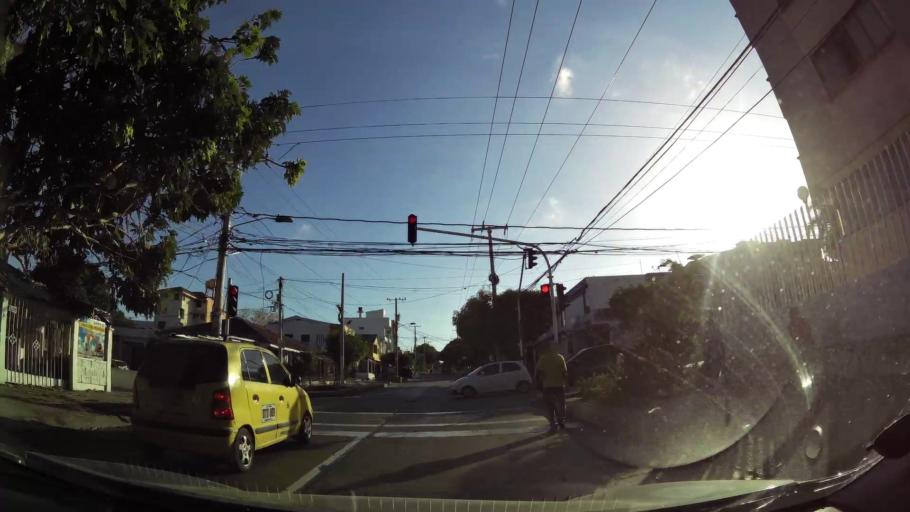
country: CO
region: Atlantico
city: Barranquilla
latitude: 10.9882
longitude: -74.8061
